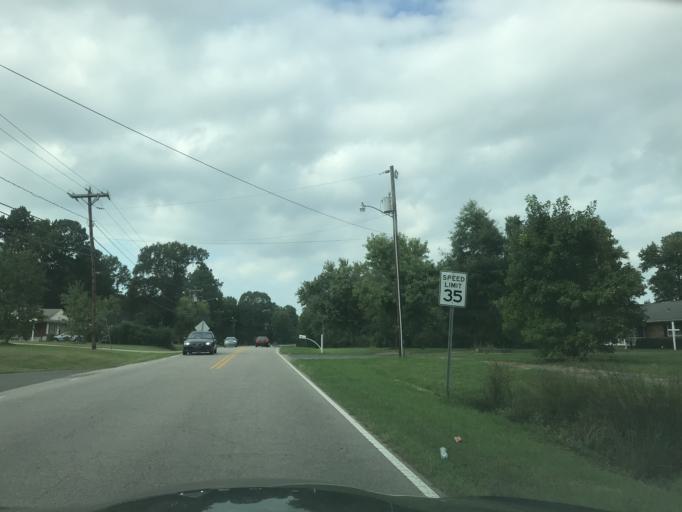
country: US
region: North Carolina
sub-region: Durham County
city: Durham
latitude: 35.9127
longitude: -78.9171
